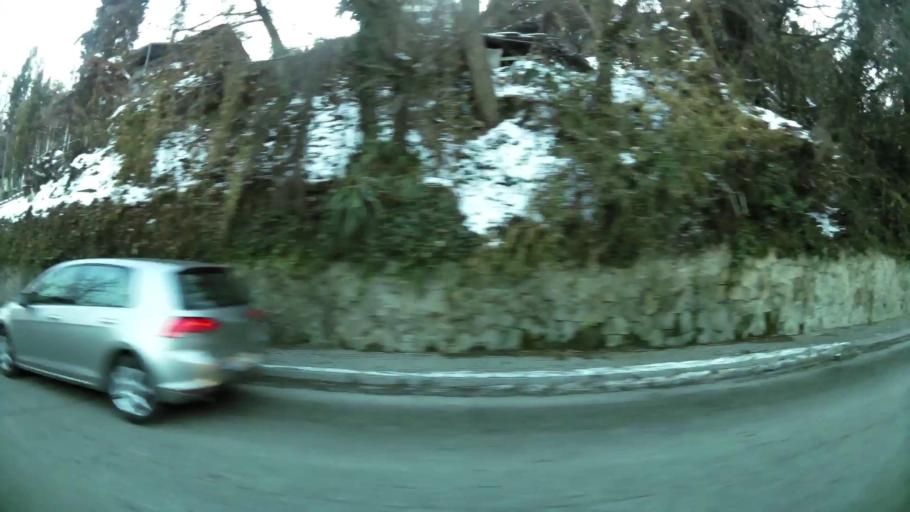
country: MK
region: Karpos
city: Skopje
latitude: 41.9926
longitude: 21.4111
